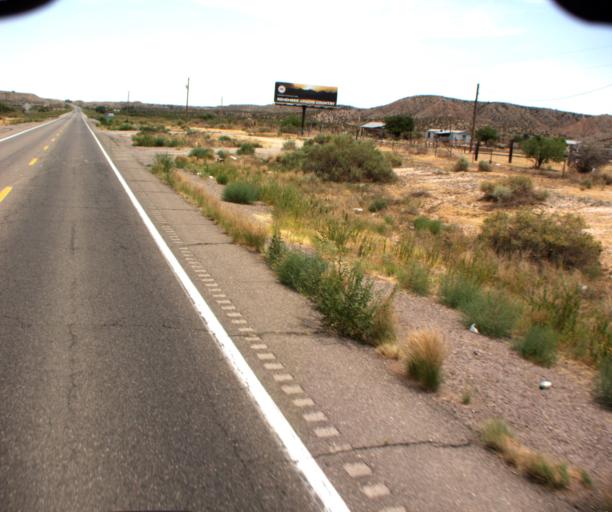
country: US
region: Arizona
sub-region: Graham County
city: Bylas
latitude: 33.0879
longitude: -110.0591
